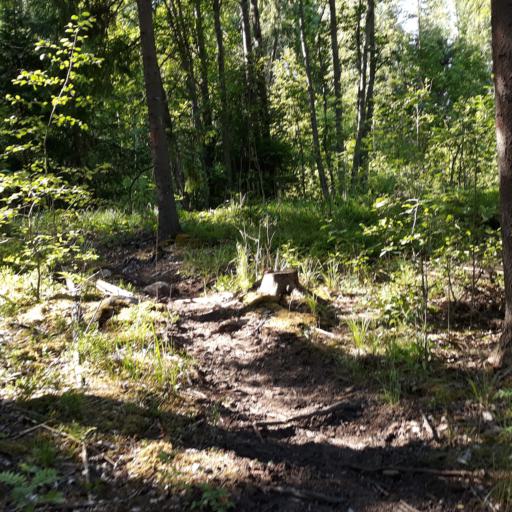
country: FI
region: Uusimaa
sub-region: Helsinki
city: Jaervenpaeae
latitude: 60.5393
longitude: 24.9842
